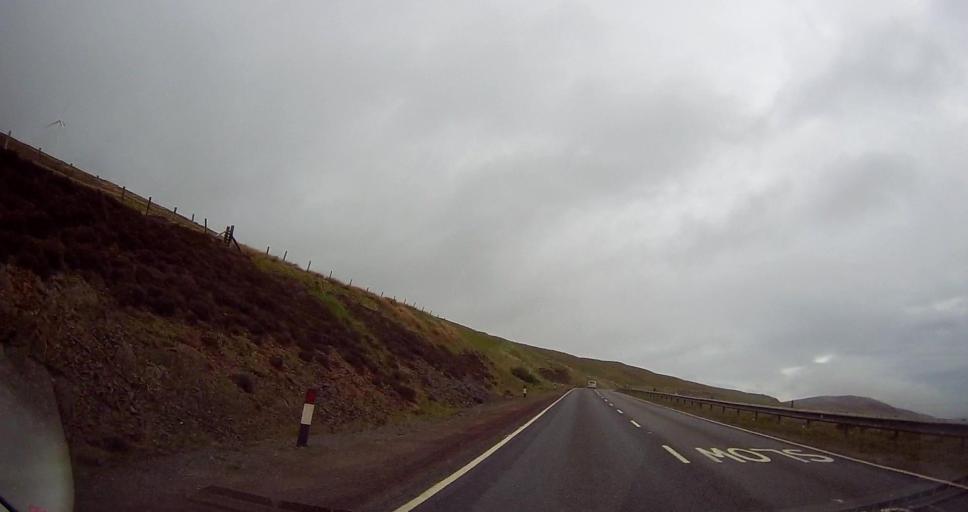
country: GB
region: Scotland
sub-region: Shetland Islands
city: Lerwick
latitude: 60.1625
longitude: -1.2270
